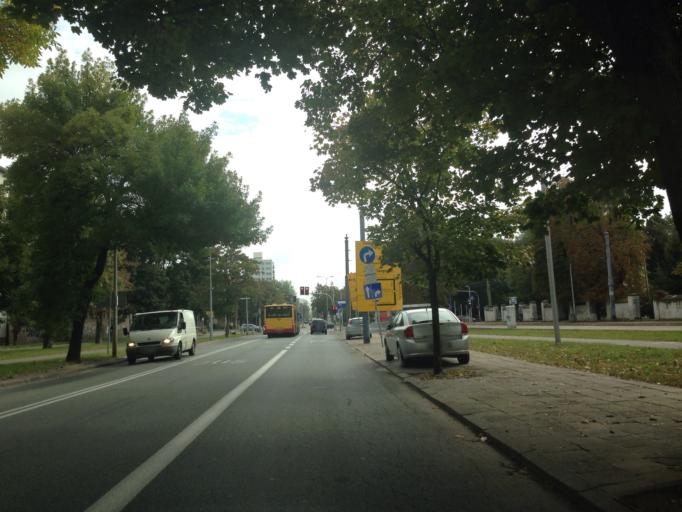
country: PL
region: Masovian Voivodeship
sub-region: Warszawa
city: Praga Polnoc
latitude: 52.2574
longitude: 21.0280
